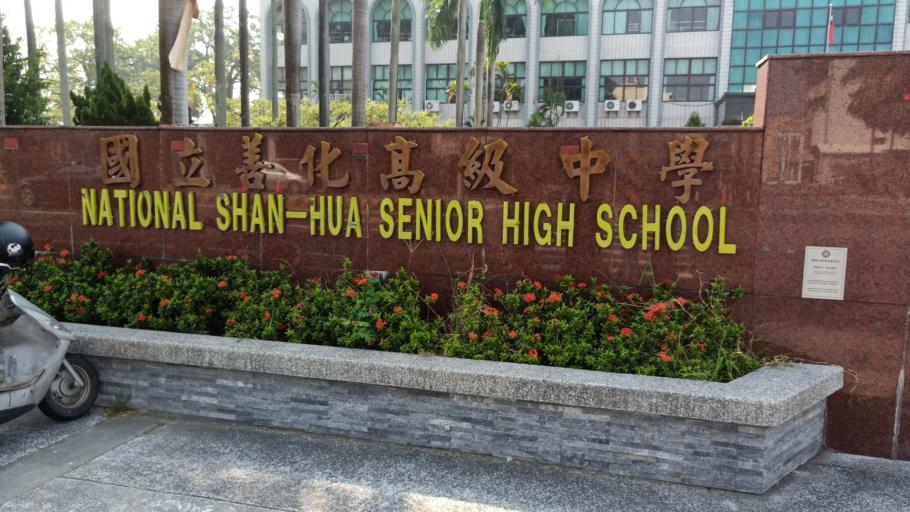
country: TW
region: Taiwan
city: Yujing
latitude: 23.1301
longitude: 120.3010
